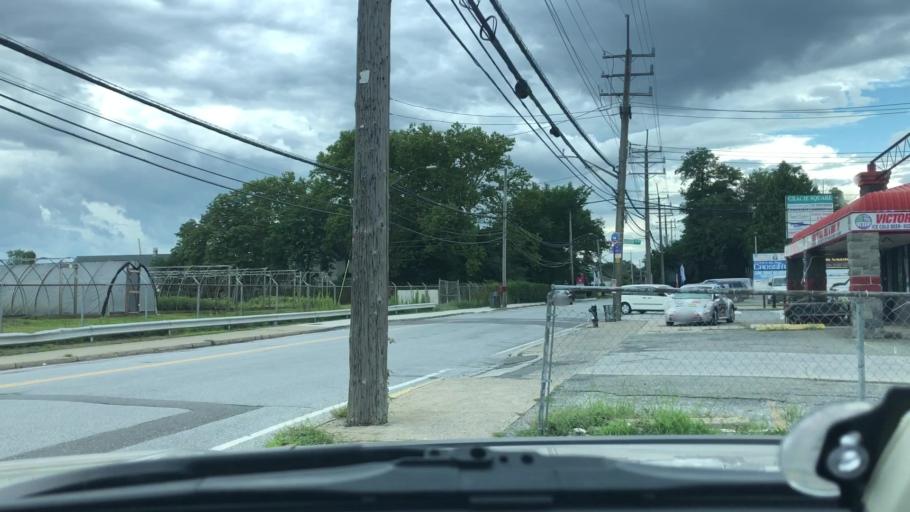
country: US
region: New York
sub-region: Richmond County
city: Bloomfield
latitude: 40.5975
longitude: -74.1817
